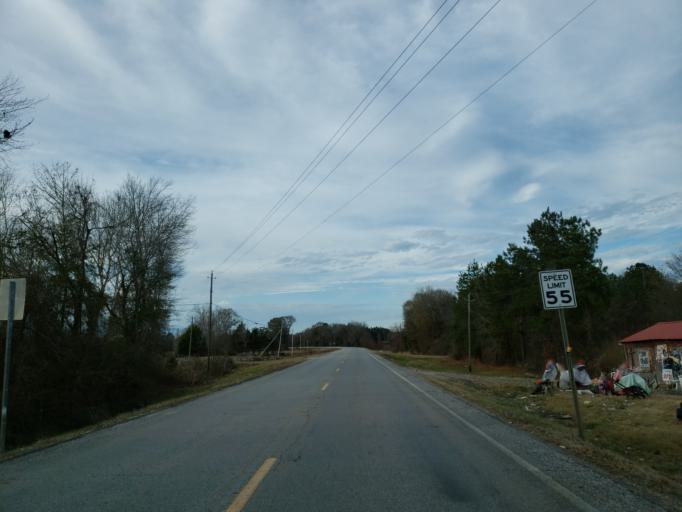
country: US
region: Mississippi
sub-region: Clarke County
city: Quitman
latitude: 31.8672
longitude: -88.7020
